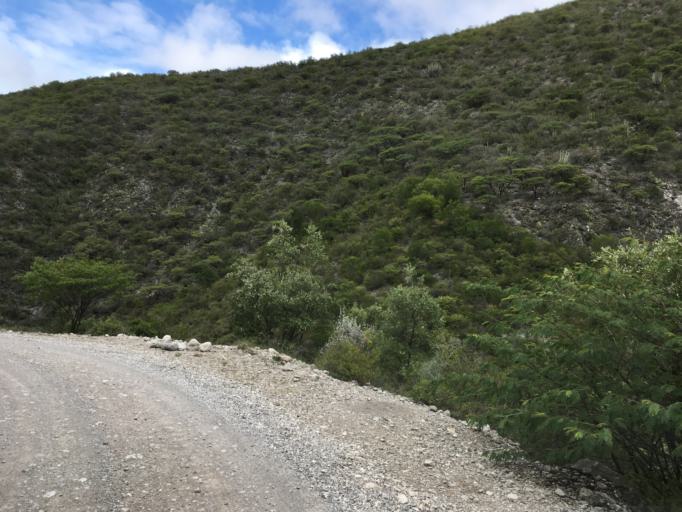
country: MX
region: Hidalgo
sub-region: Metztitlan
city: Fontezuelas
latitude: 20.6235
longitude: -98.8849
